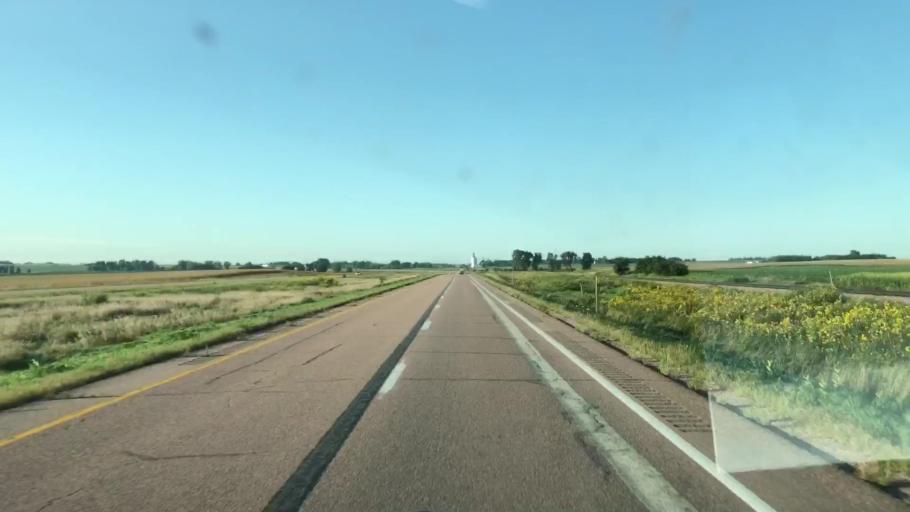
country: US
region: Iowa
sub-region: Osceola County
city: Sibley
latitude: 43.3422
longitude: -95.7754
